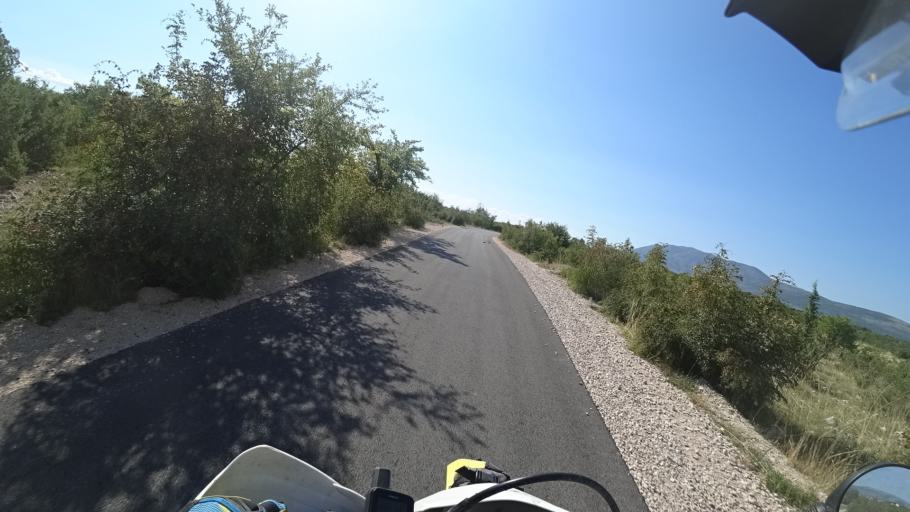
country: HR
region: Sibensko-Kniniska
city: Knin
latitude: 44.0034
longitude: 16.1939
